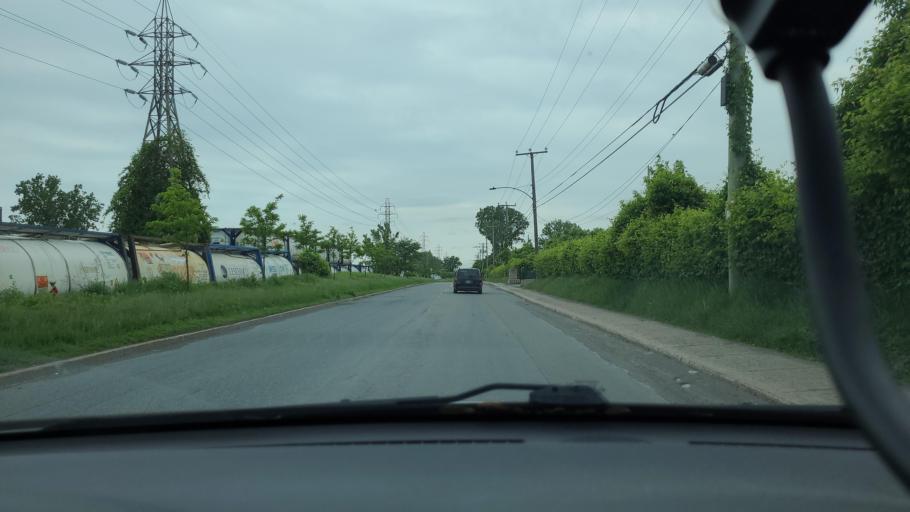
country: CA
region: Quebec
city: Cote-Saint-Luc
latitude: 45.4480
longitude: -73.6679
